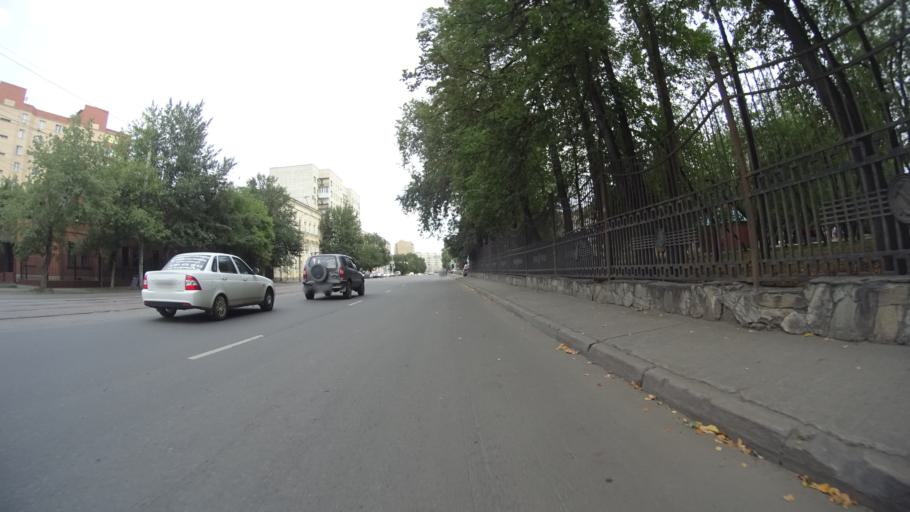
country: RU
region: Chelyabinsk
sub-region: Gorod Chelyabinsk
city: Chelyabinsk
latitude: 55.1538
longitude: 61.4080
